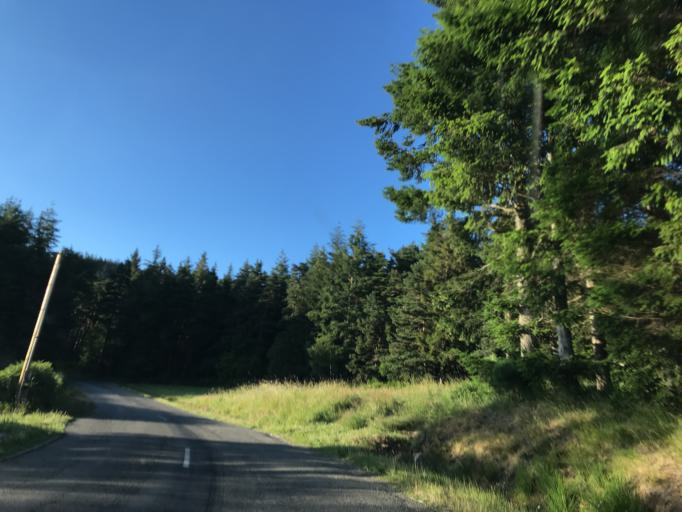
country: FR
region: Rhone-Alpes
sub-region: Departement de la Loire
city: Sail-sous-Couzan
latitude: 45.7158
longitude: 3.8613
